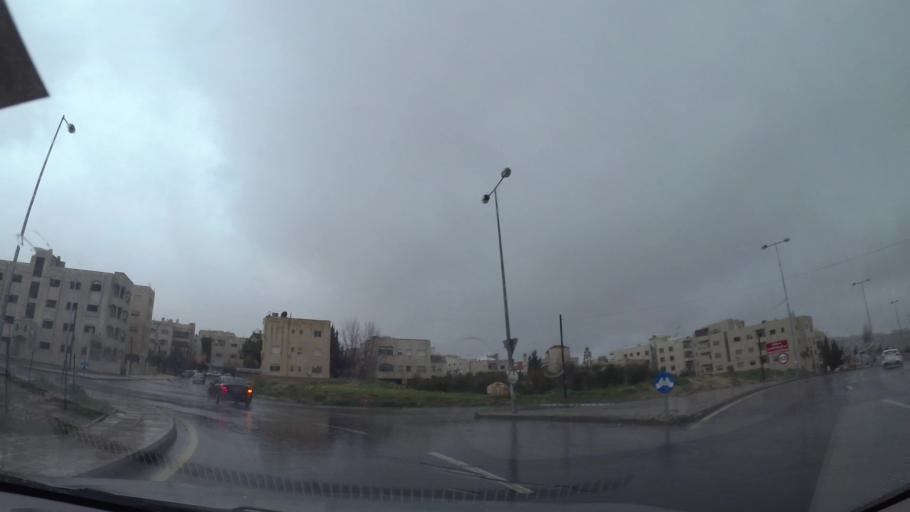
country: JO
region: Amman
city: Al Jubayhah
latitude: 32.0348
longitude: 35.8834
